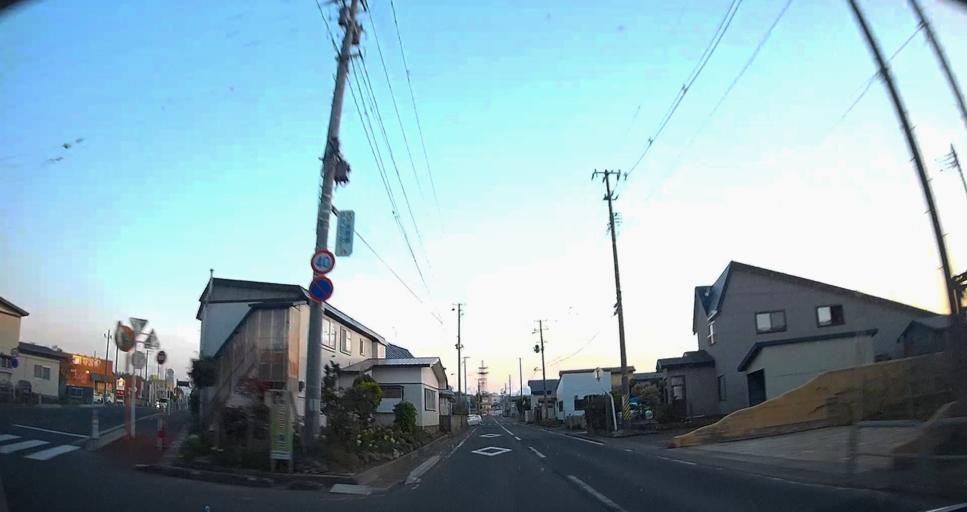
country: JP
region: Aomori
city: Misawa
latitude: 40.8702
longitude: 141.1315
